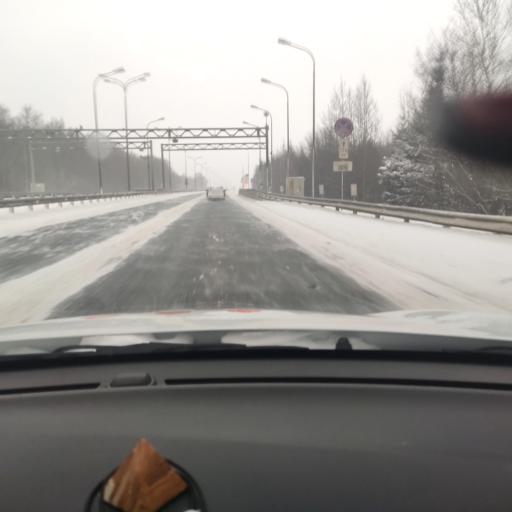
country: RU
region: Tatarstan
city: Sviyazhsk
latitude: 55.7495
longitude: 48.7994
